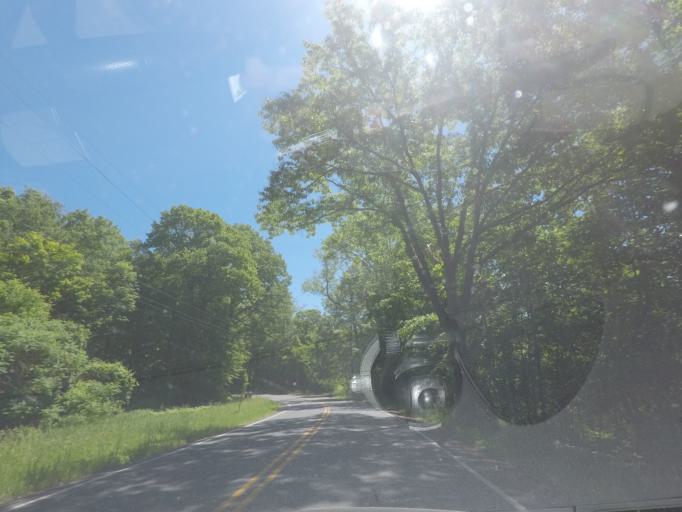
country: US
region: New York
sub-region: Saratoga County
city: Country Knolls
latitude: 42.9434
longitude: -73.7626
